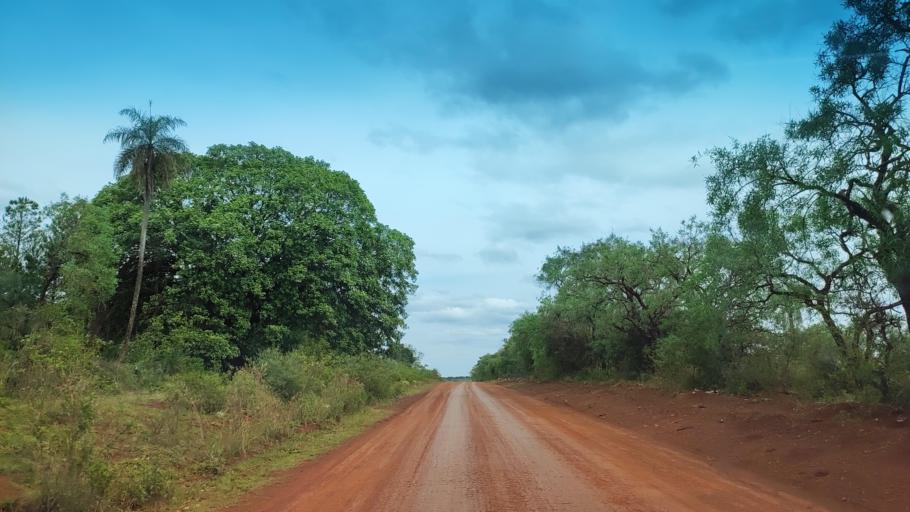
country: AR
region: Misiones
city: Garupa
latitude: -27.5115
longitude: -55.9705
